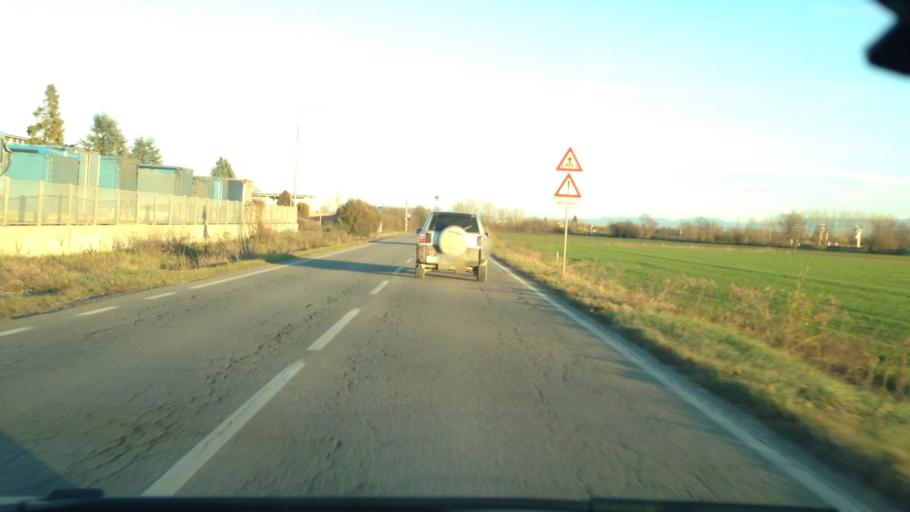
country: IT
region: Piedmont
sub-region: Provincia di Alessandria
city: Solero
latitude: 44.9209
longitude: 8.5249
